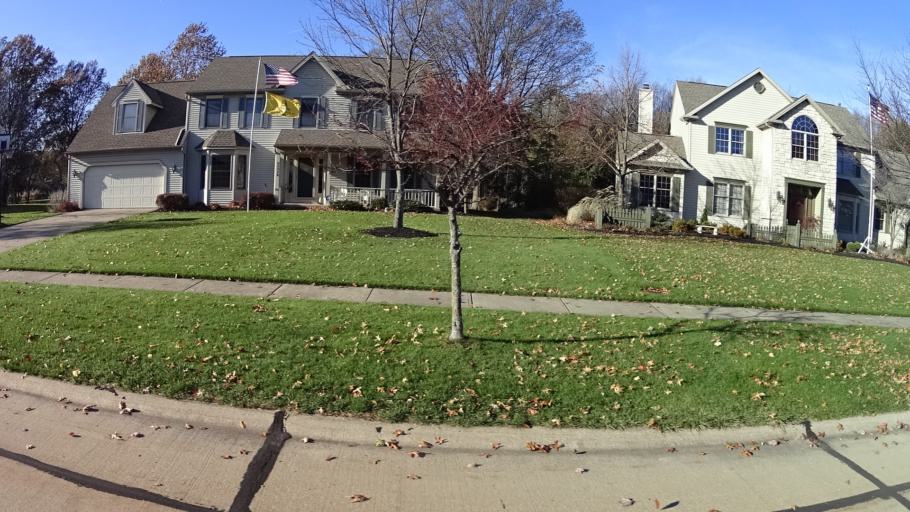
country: US
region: Ohio
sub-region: Lorain County
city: Avon Lake
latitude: 41.5028
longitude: -81.9996
